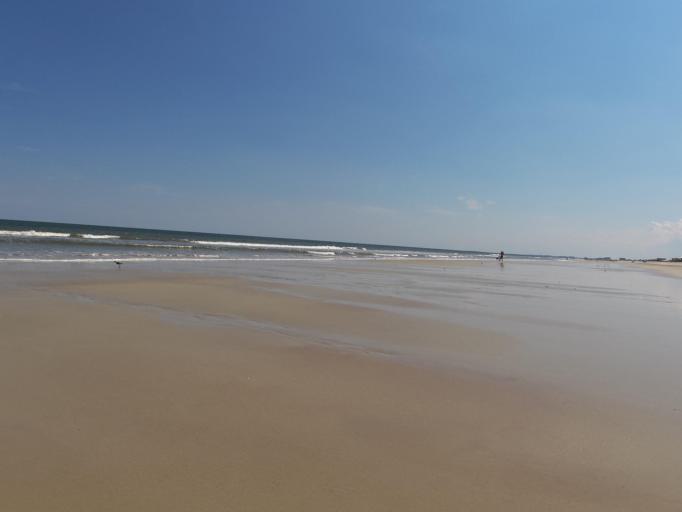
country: US
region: Florida
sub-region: Nassau County
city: Fernandina Beach
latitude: 30.6528
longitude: -81.4324
